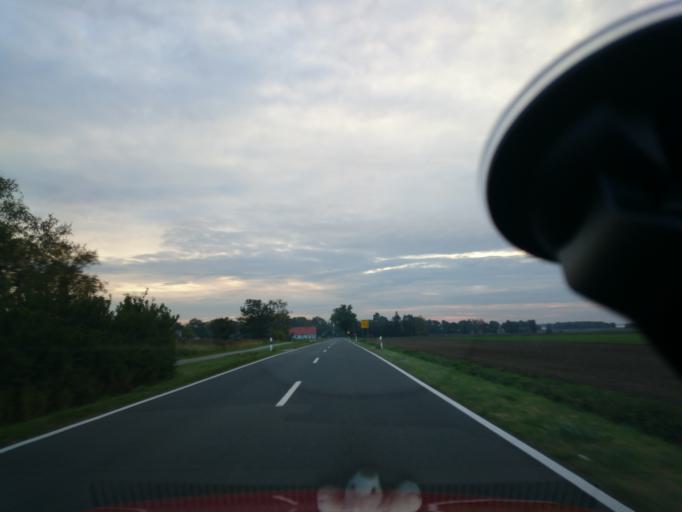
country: DE
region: Mecklenburg-Vorpommern
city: Saal
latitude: 54.3159
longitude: 12.4989
